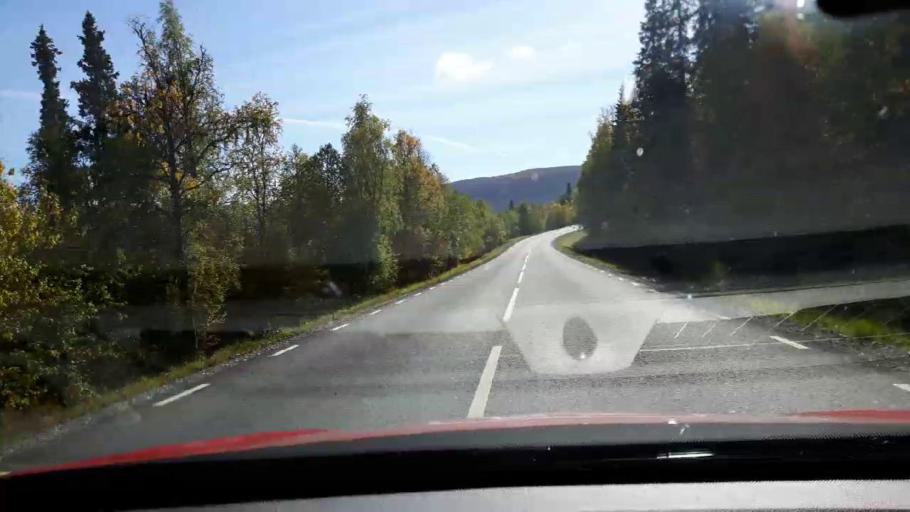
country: NO
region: Nord-Trondelag
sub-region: Royrvik
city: Royrvik
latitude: 64.8765
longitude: 14.2118
